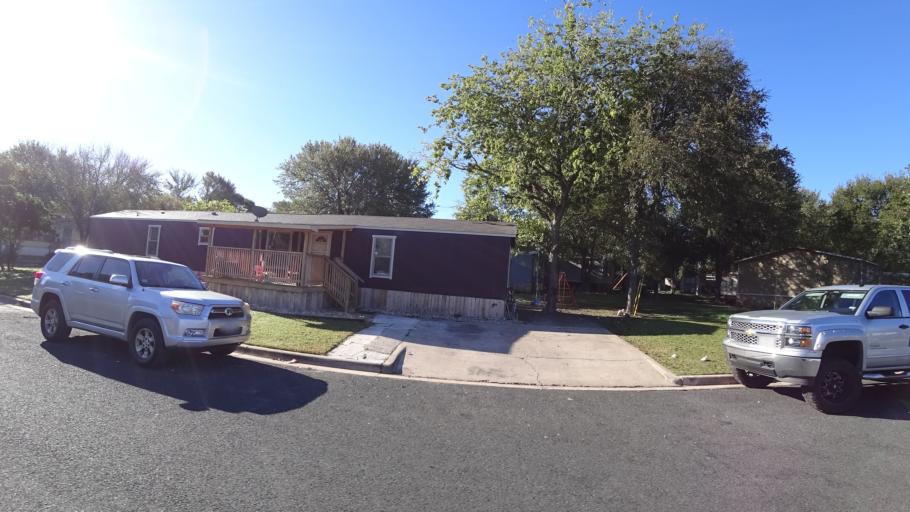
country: US
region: Texas
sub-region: Travis County
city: Austin
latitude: 30.2249
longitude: -97.6704
